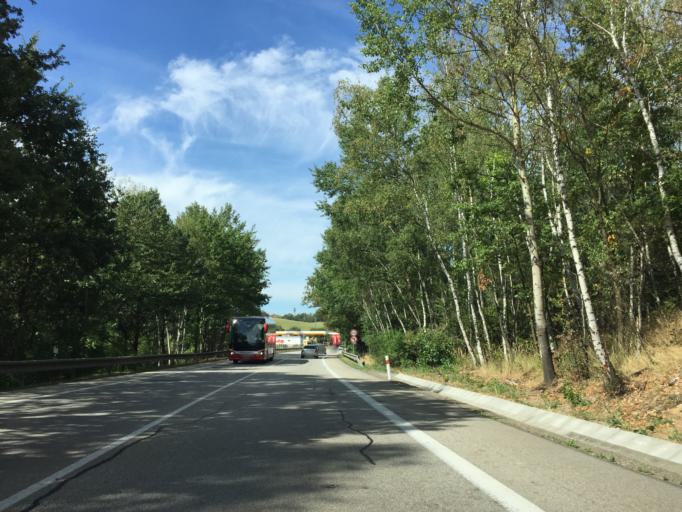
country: CZ
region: Central Bohemia
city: Votice
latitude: 49.6529
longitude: 14.6333
